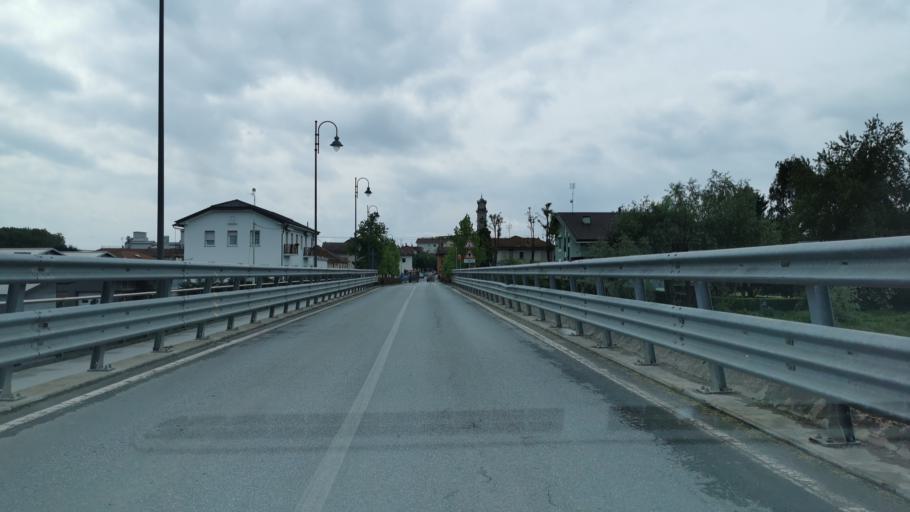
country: IT
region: Piedmont
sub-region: Provincia di Cuneo
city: Villafalletto
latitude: 44.5484
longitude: 7.5385
